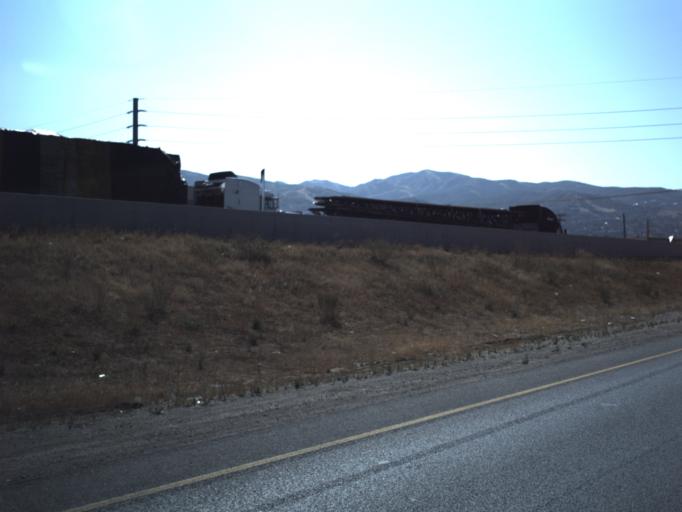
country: US
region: Utah
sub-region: Davis County
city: West Bountiful
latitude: 40.8831
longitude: -111.8972
